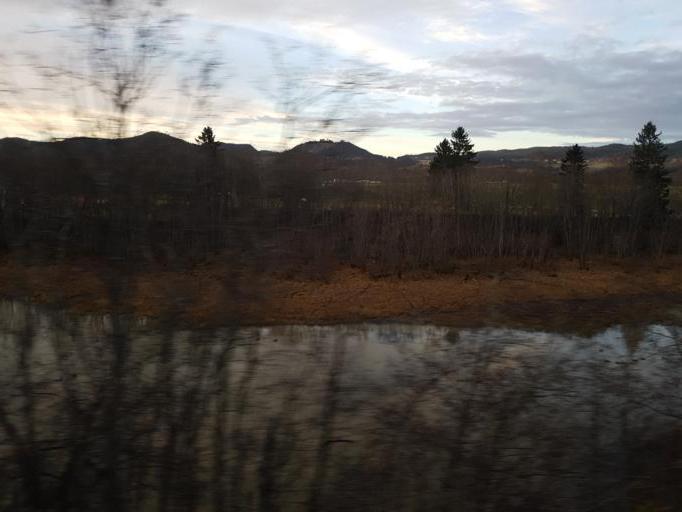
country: NO
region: Sor-Trondelag
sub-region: Melhus
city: Melhus
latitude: 63.2222
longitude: 10.2909
